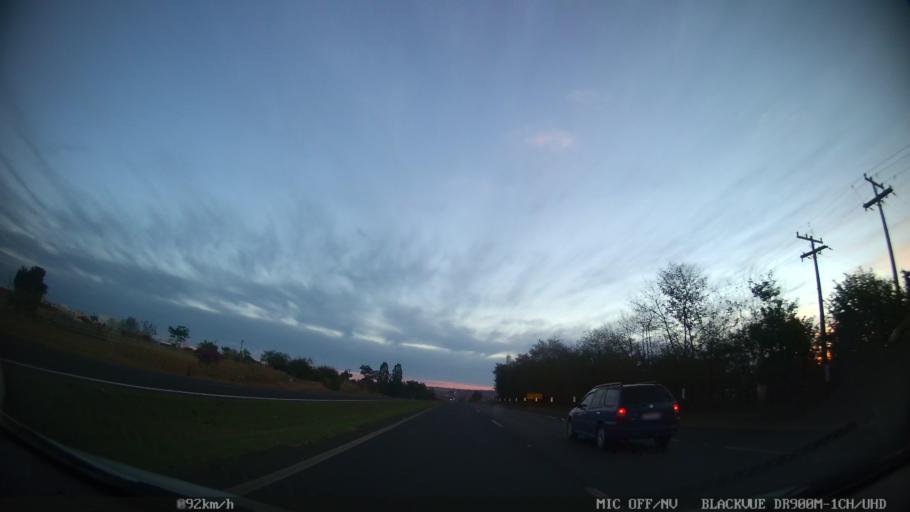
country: BR
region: Sao Paulo
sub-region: Catanduva
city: Catanduva
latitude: -21.1102
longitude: -48.9660
